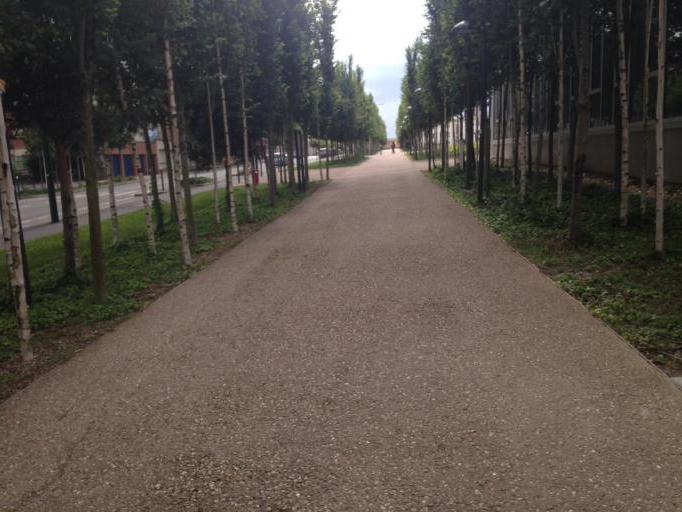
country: FR
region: Nord-Pas-de-Calais
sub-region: Departement du Pas-de-Calais
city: Lens
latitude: 50.4287
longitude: 2.8249
